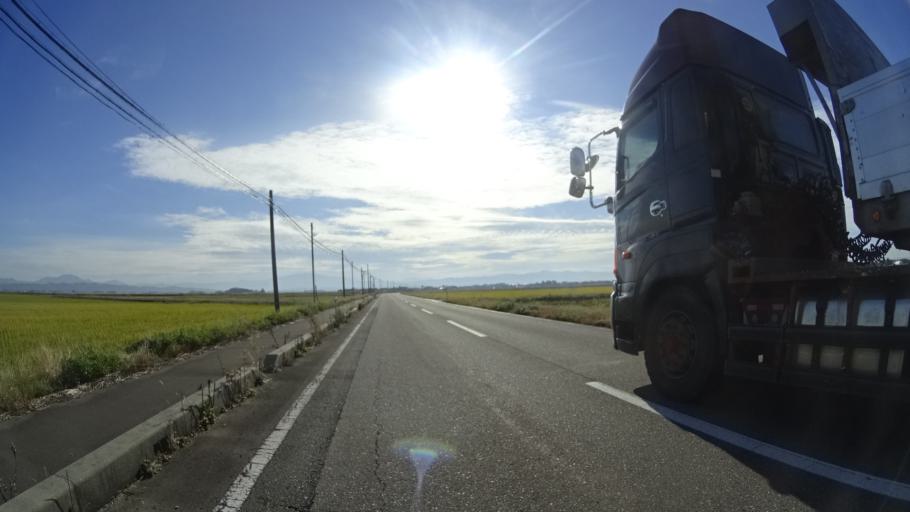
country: JP
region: Niigata
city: Mitsuke
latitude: 37.5683
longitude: 138.8438
